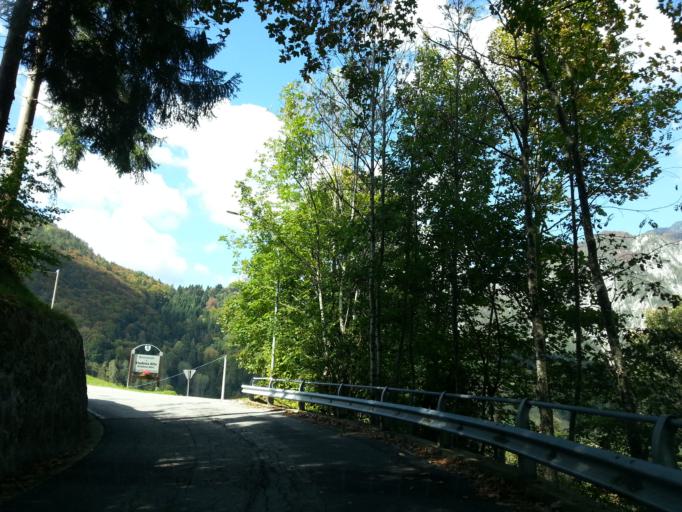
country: IT
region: Friuli Venezia Giulia
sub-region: Provincia di Udine
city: Pontebba
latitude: 46.5089
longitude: 13.2839
